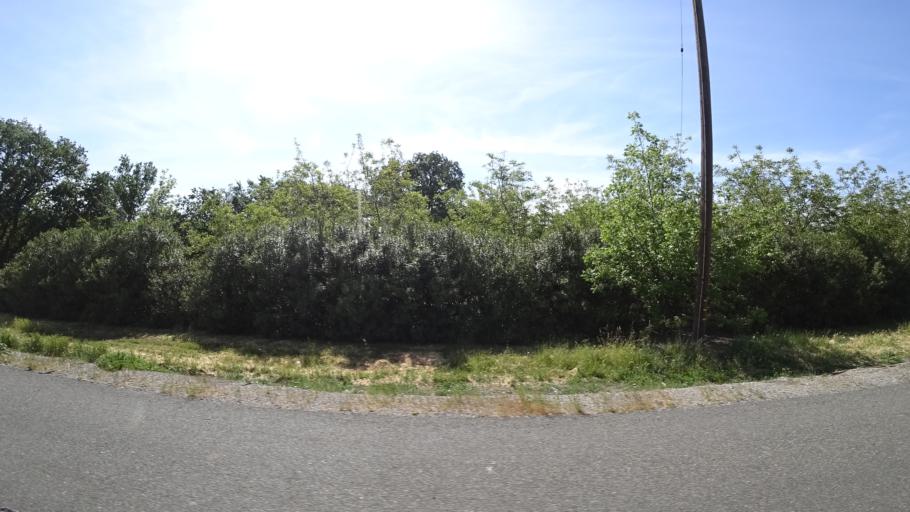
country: US
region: California
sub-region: Tehama County
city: Gerber
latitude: 40.0756
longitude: -122.1007
